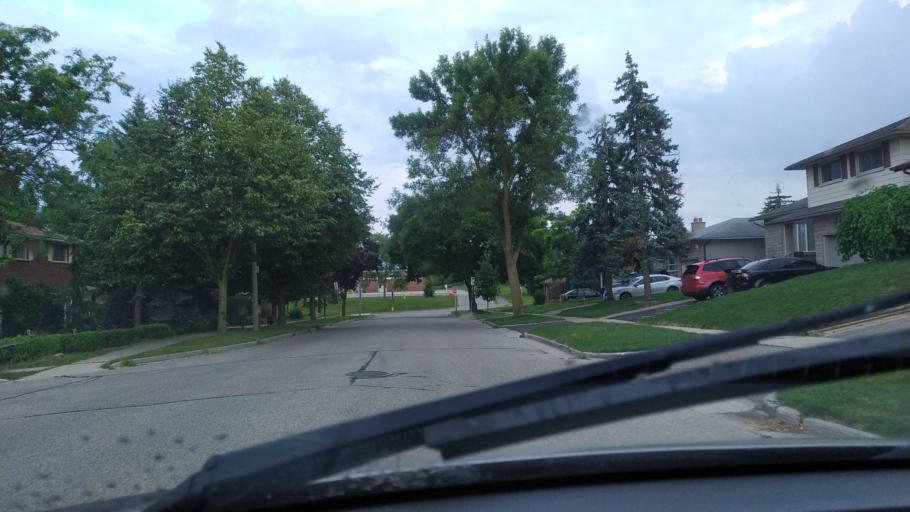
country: CA
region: Ontario
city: Kitchener
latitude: 43.4306
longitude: -80.5201
